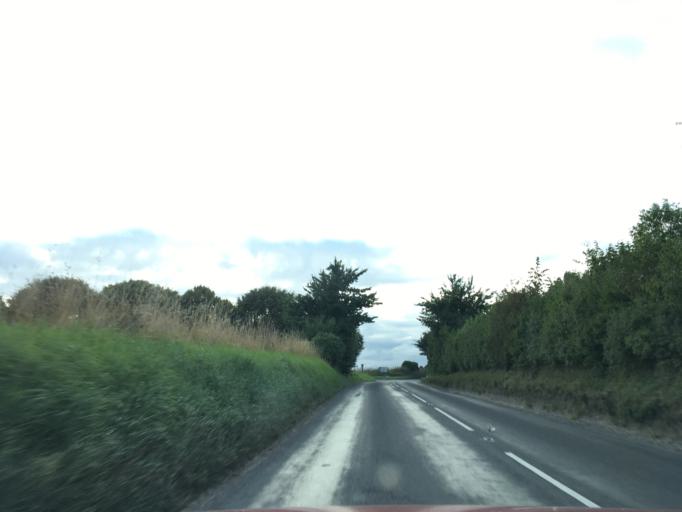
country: GB
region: England
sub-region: Wiltshire
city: Wilsford
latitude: 51.3147
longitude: -1.9131
